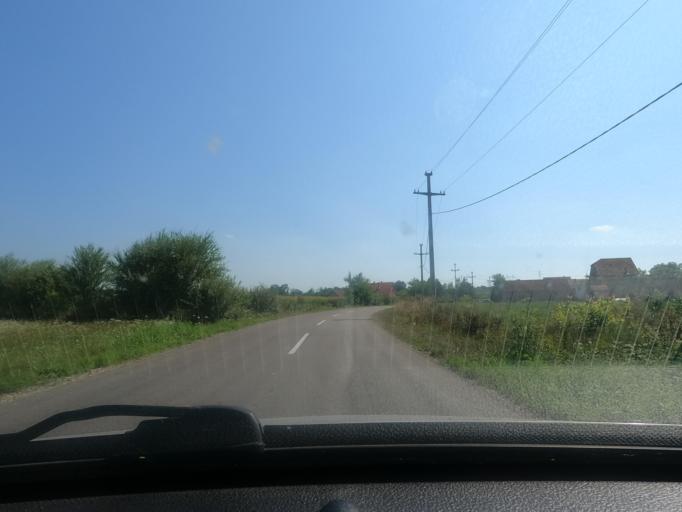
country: RS
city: Kozjak
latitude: 44.5483
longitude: 19.3088
